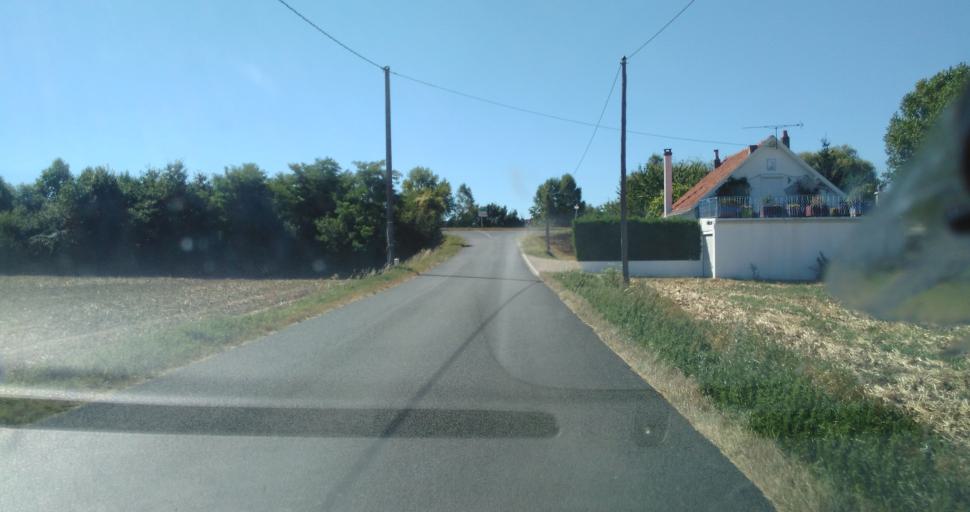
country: FR
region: Centre
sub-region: Departement d'Indre-et-Loire
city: Vernou-sur-Brenne
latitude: 47.4013
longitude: 0.8555
